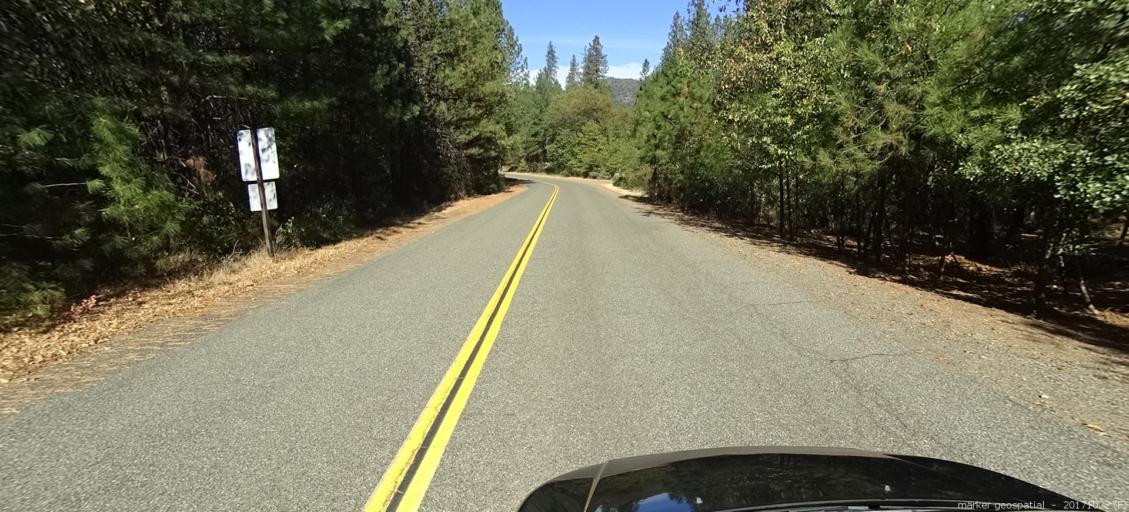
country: US
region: California
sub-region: Shasta County
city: Central Valley (historical)
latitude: 40.9097
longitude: -122.3838
